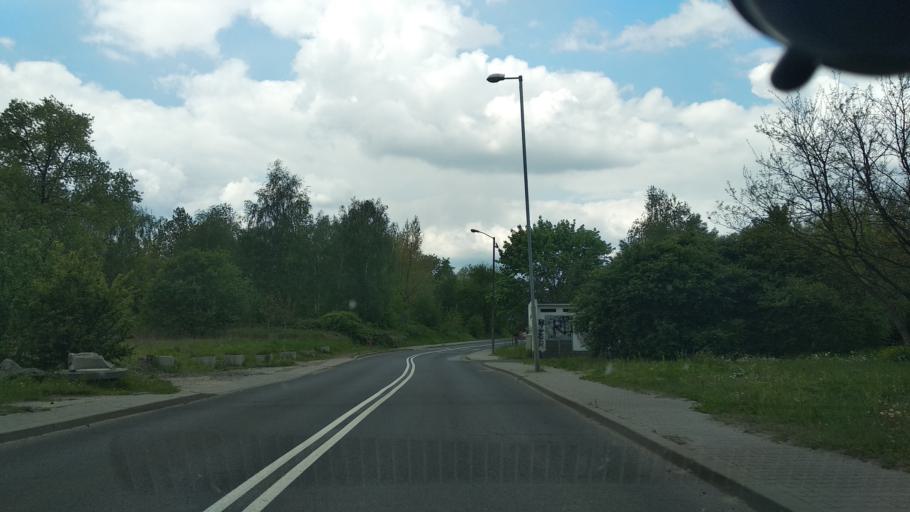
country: PL
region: Silesian Voivodeship
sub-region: Katowice
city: Katowice
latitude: 50.2590
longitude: 18.9824
